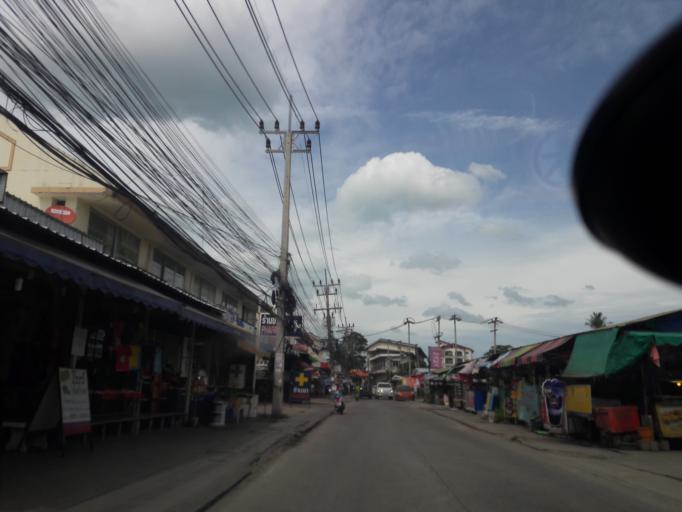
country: TH
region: Surat Thani
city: Ko Samui
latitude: 9.5212
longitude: 100.0530
